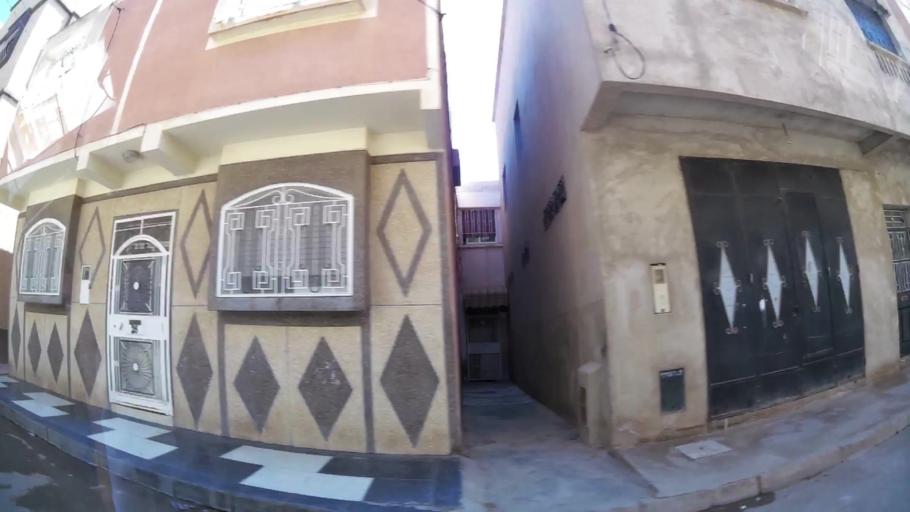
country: MA
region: Oriental
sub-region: Oujda-Angad
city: Oujda
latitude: 34.6687
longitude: -1.9452
